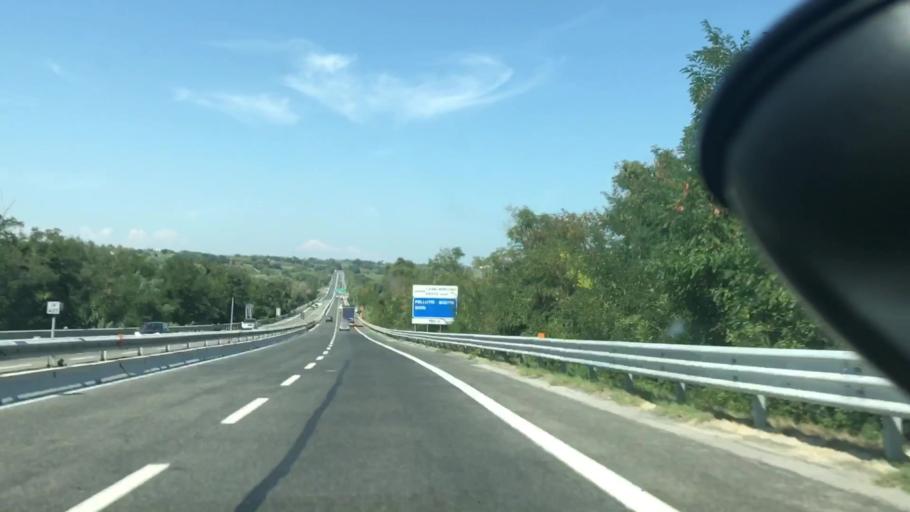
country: IT
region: Abruzzo
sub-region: Provincia di Chieti
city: Casalbordino-Miracoli
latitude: 42.1543
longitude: 14.6500
